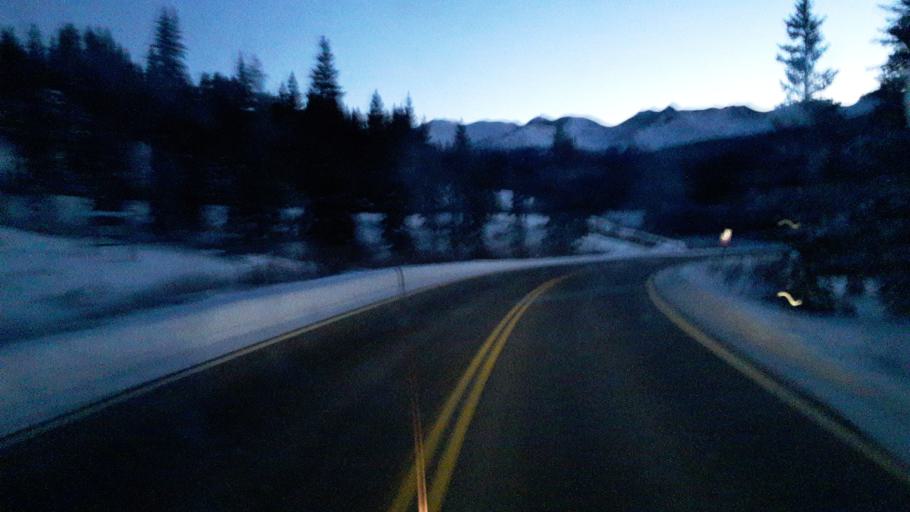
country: US
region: Colorado
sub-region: San Juan County
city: Silverton
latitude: 37.7474
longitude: -107.6932
